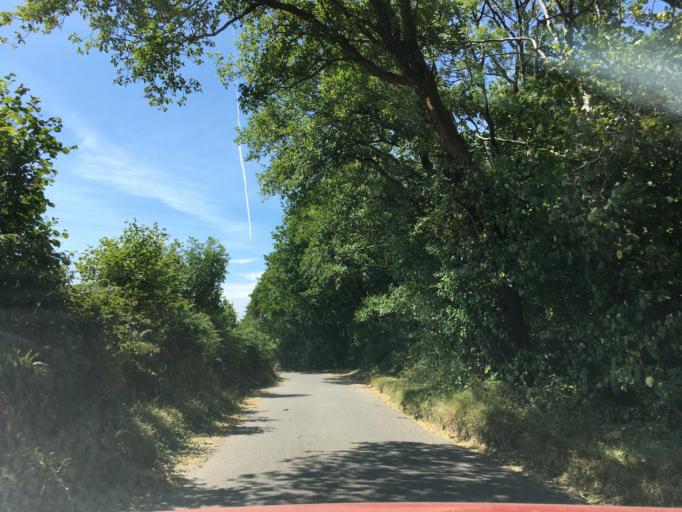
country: GB
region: Wales
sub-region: Caerphilly County Borough
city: Machen
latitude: 51.5568
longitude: -3.1471
